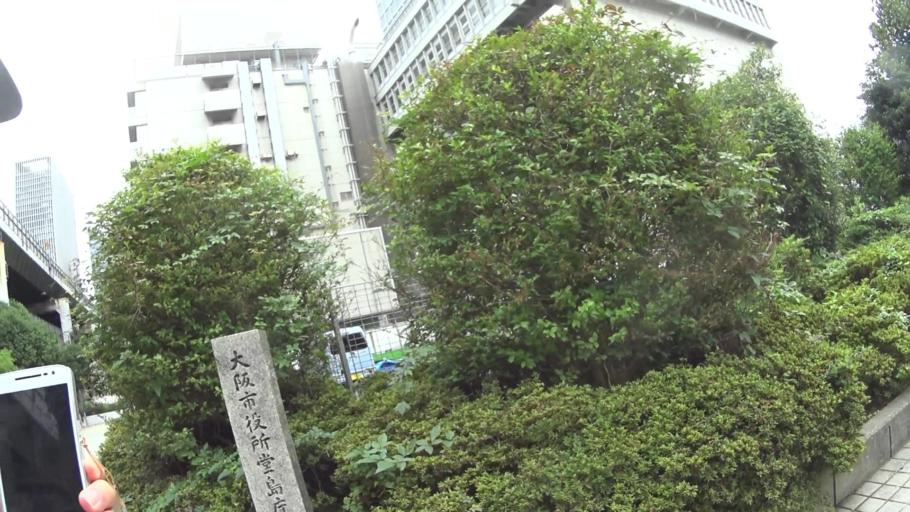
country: JP
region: Osaka
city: Osaka-shi
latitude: 34.6965
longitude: 135.4916
